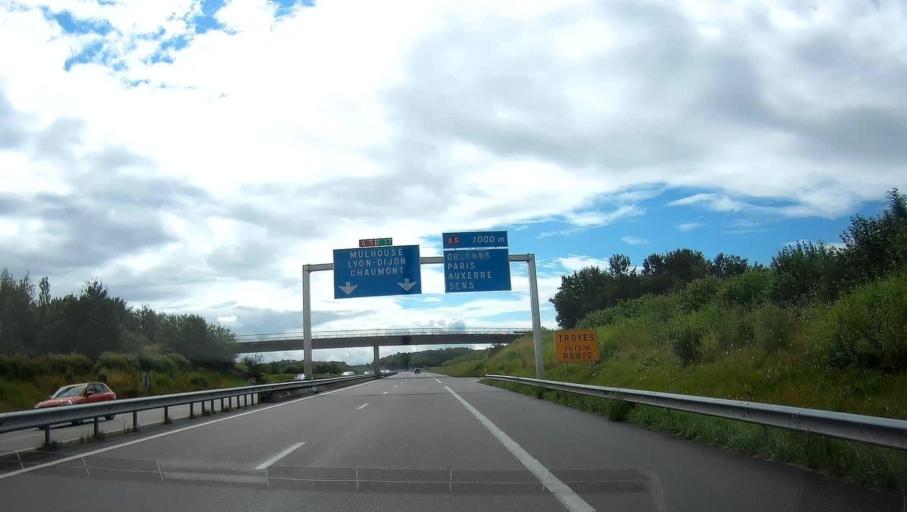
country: FR
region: Champagne-Ardenne
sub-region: Departement de l'Aube
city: Verrieres
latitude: 48.2422
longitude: 4.1706
